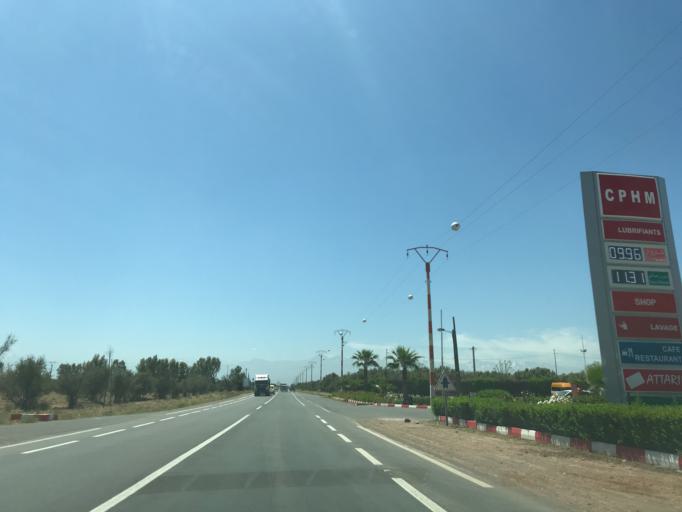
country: MA
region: Marrakech-Tensift-Al Haouz
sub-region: Marrakech
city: Marrakesh
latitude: 31.5448
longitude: -8.0030
